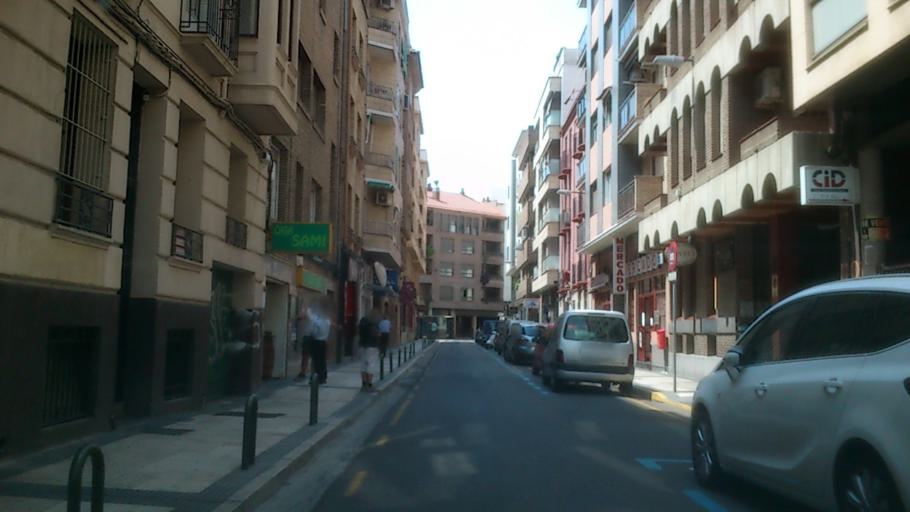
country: ES
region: Aragon
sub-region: Provincia de Zaragoza
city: Zaragoza
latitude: 41.6437
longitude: -0.8831
